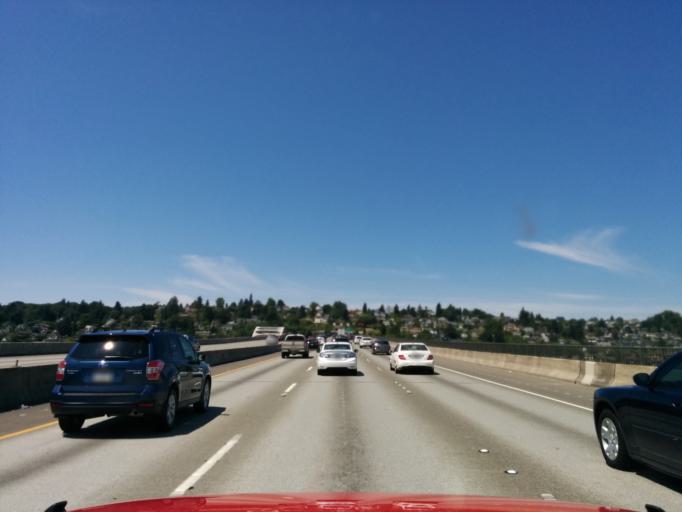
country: US
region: Washington
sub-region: King County
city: Seattle
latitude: 47.5901
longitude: -122.2785
